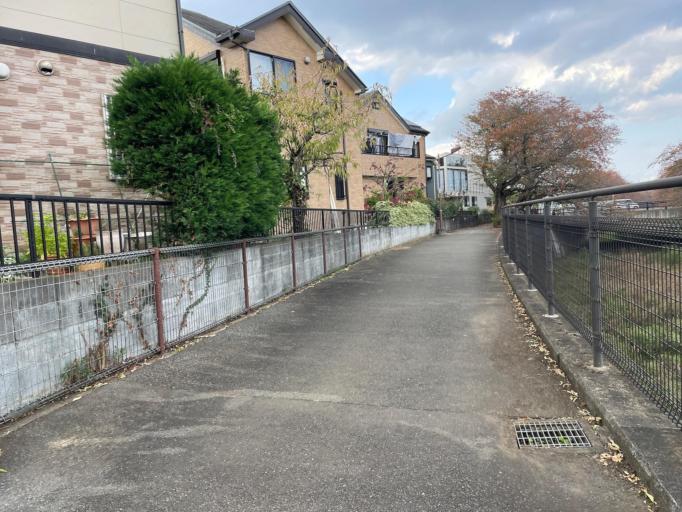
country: JP
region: Tokyo
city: Hino
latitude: 35.7219
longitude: 139.3846
